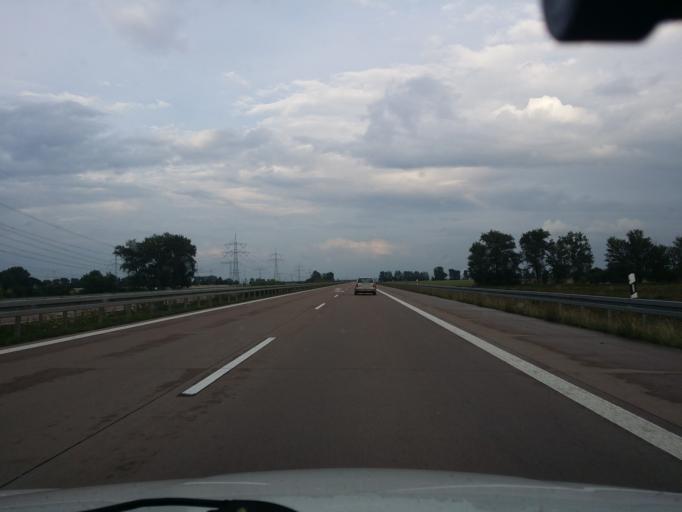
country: DE
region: Saxony-Anhalt
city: Schafstadt
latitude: 51.4033
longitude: 11.7964
